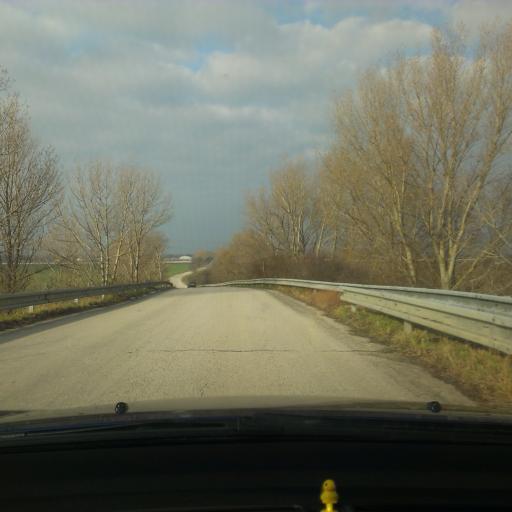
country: SK
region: Trnavsky
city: Leopoldov
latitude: 48.5196
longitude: 17.7870
